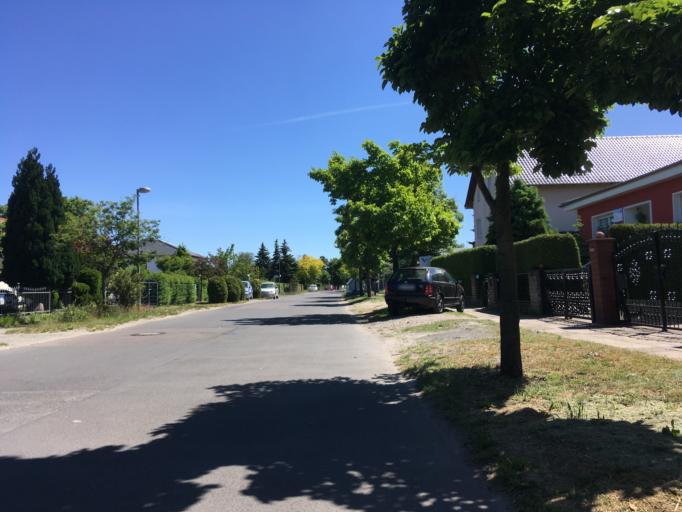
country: DE
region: Berlin
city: Berlin Koepenick
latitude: 52.4358
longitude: 13.5897
